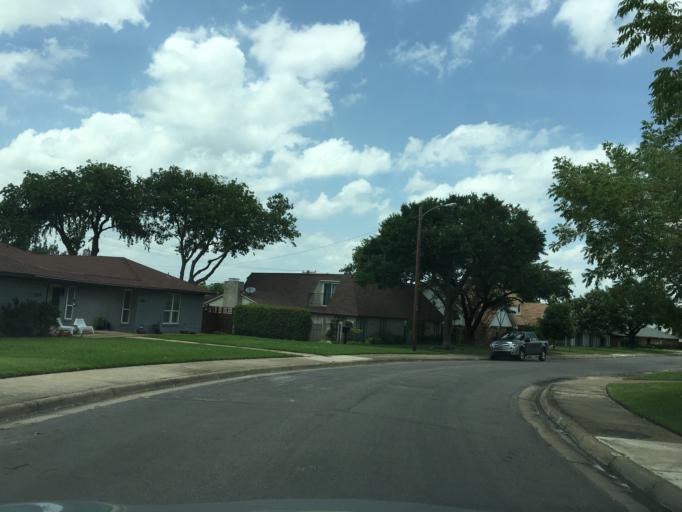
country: US
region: Texas
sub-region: Dallas County
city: University Park
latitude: 32.8901
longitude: -96.7805
